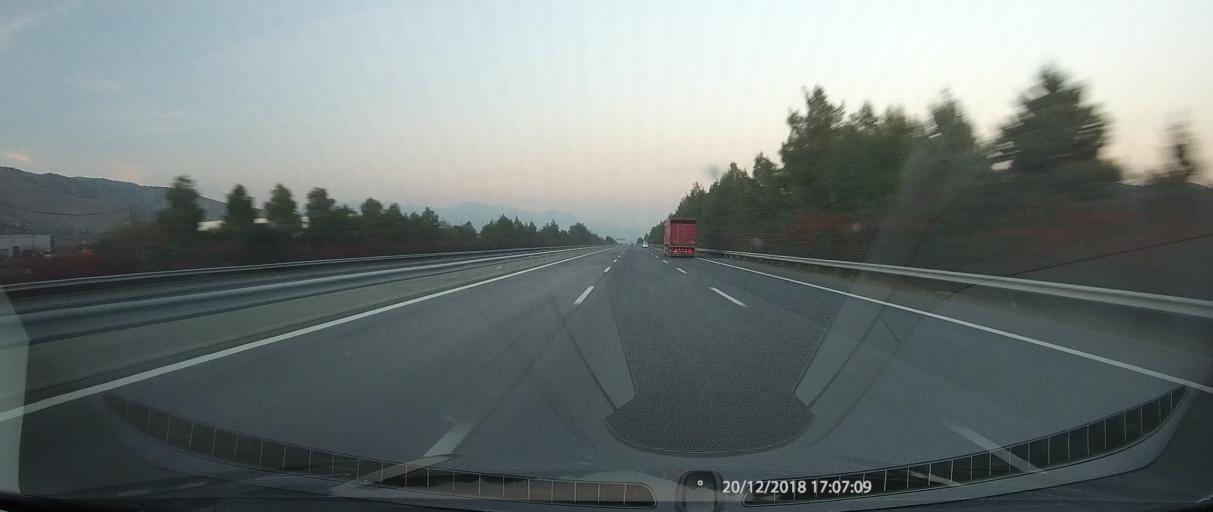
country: GR
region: Thessaly
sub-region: Nomos Larisis
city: Makrychori
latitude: 39.7720
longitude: 22.4851
